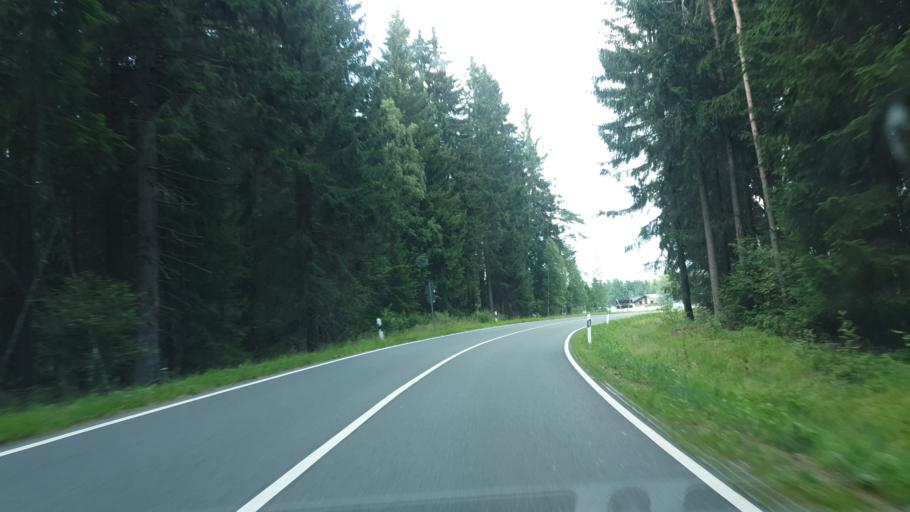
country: DE
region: Saxony
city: Hammerbrucke
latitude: 50.4482
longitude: 12.4239
